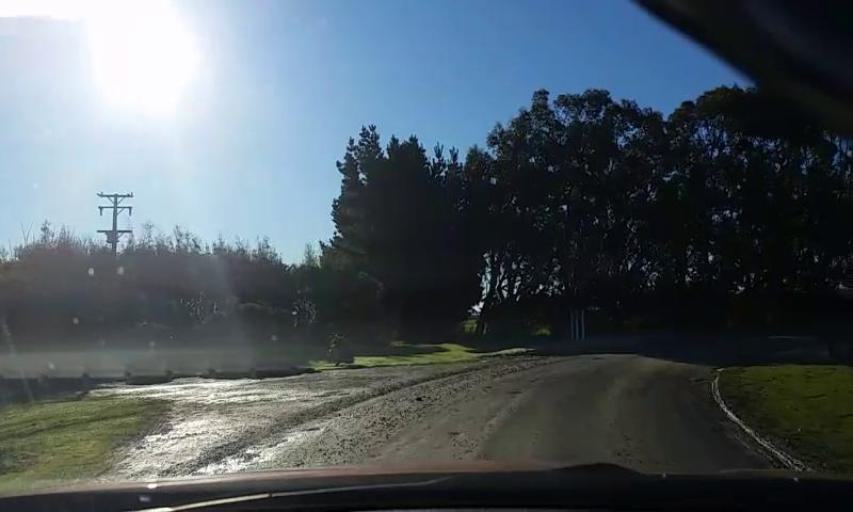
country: NZ
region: Southland
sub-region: Invercargill City
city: Invercargill
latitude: -46.3562
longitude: 168.4320
